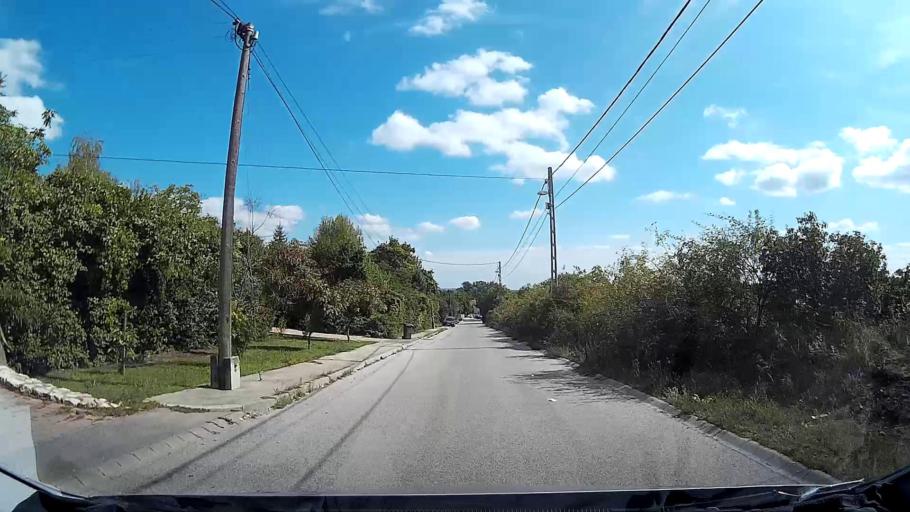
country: HU
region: Pest
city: Szentendre
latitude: 47.6862
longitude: 19.0652
